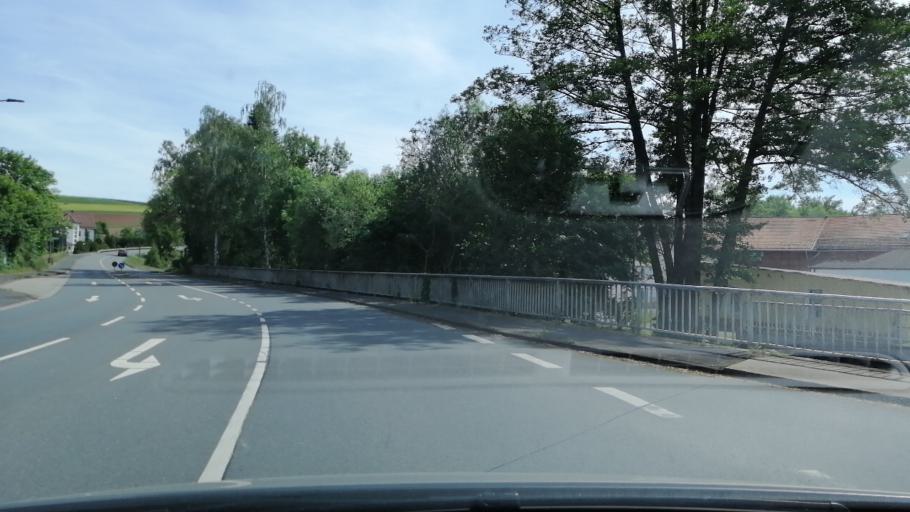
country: DE
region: Hesse
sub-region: Regierungsbezirk Kassel
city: Bad Wildungen
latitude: 51.1549
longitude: 9.1213
